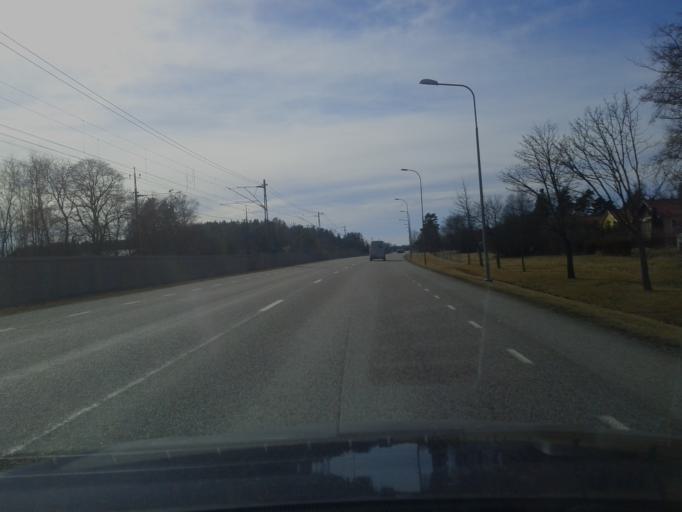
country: SE
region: Soedermanland
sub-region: Eskilstuna Kommun
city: Kvicksund
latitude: 59.5707
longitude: 16.3865
